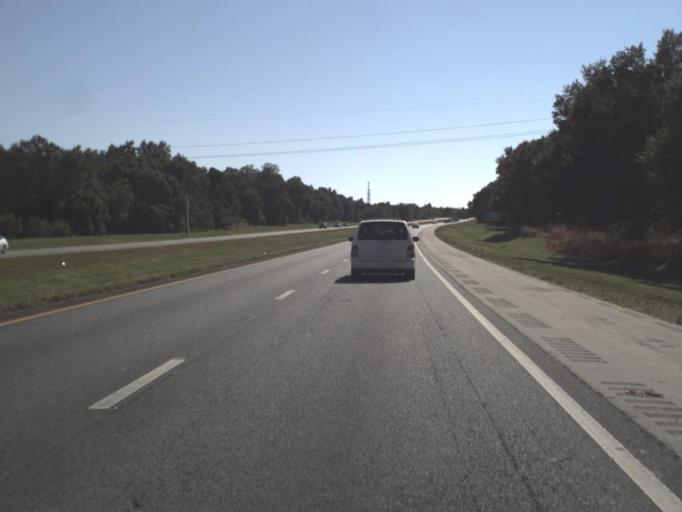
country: US
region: Florida
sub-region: Seminole County
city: Oviedo
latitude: 28.6760
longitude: -81.2262
